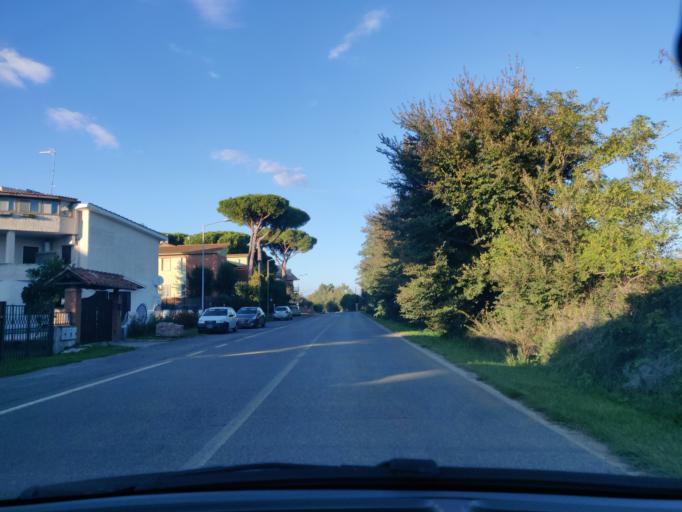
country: IT
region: Latium
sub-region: Provincia di Viterbo
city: Tarquinia
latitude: 42.2213
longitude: 11.7158
